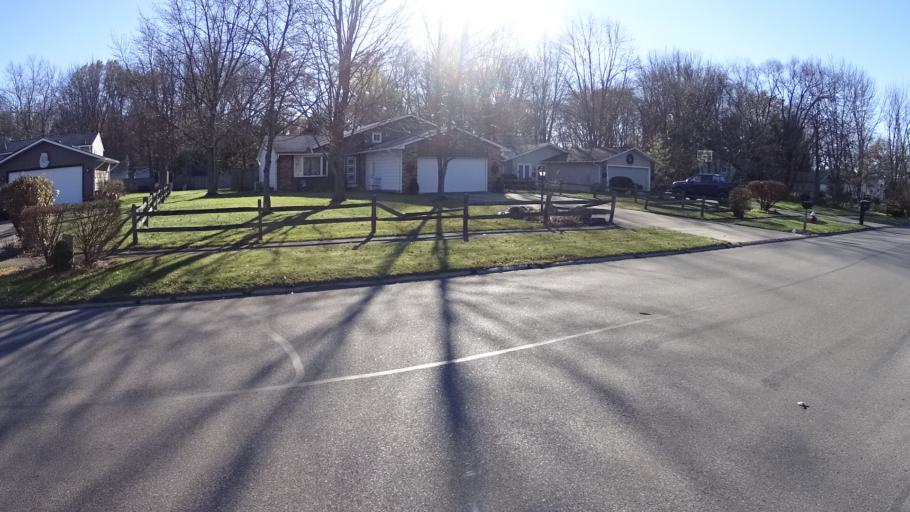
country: US
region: Ohio
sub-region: Lorain County
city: North Ridgeville
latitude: 41.3996
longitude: -82.0161
